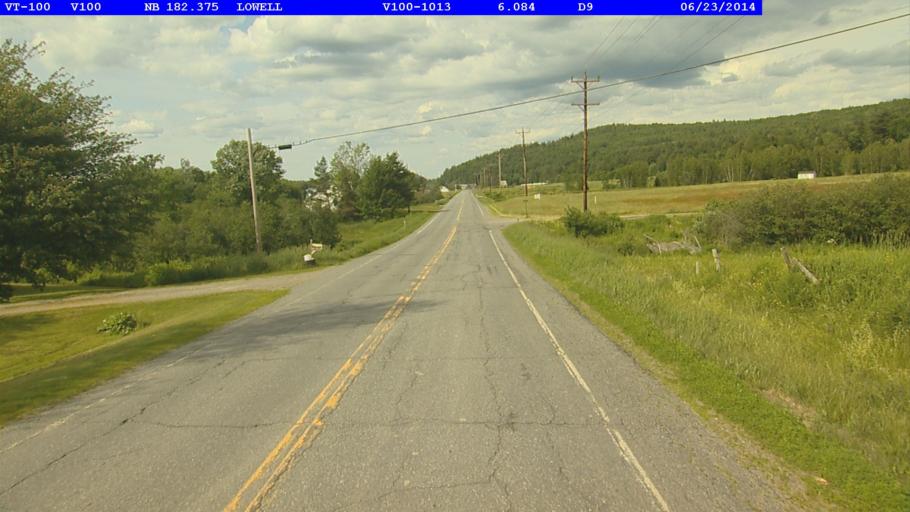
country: US
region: Vermont
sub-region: Orleans County
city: Newport
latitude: 44.8226
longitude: -72.4390
